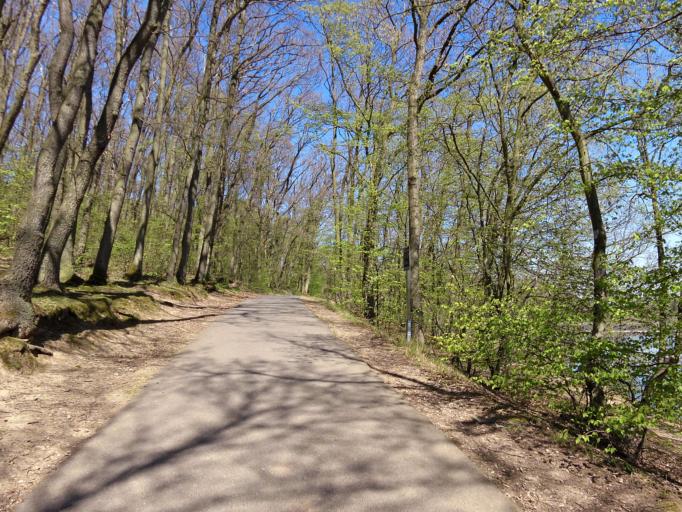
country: DE
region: North Rhine-Westphalia
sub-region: Regierungsbezirk Koln
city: Bad Munstereifel
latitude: 50.5931
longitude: 6.8361
